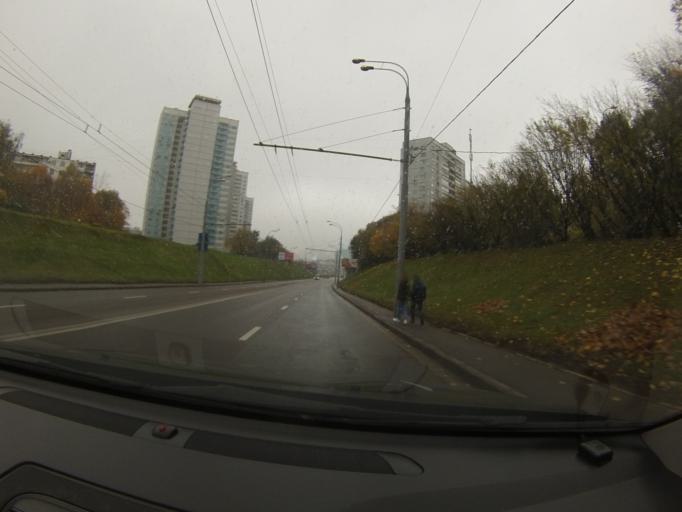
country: RU
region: Moscow
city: Troparevo
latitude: 55.6595
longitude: 37.4880
